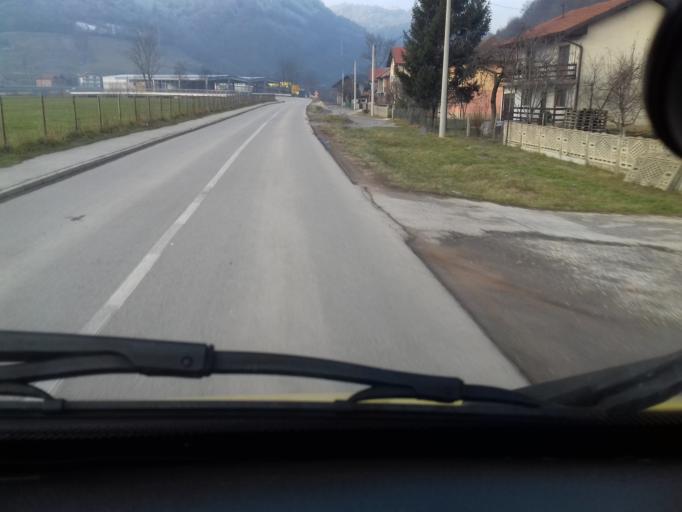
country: BA
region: Federation of Bosnia and Herzegovina
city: Dobrinje
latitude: 44.0533
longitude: 18.1071
